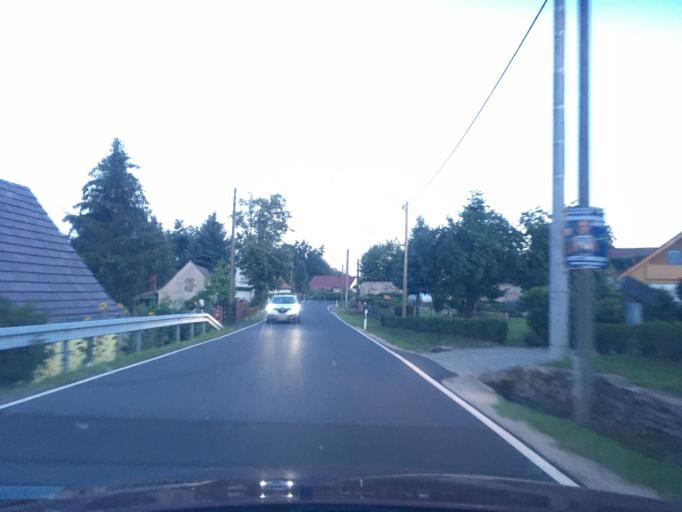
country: PL
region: Lower Silesian Voivodeship
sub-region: Powiat zgorzelecki
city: Piensk
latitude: 51.2200
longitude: 15.0039
